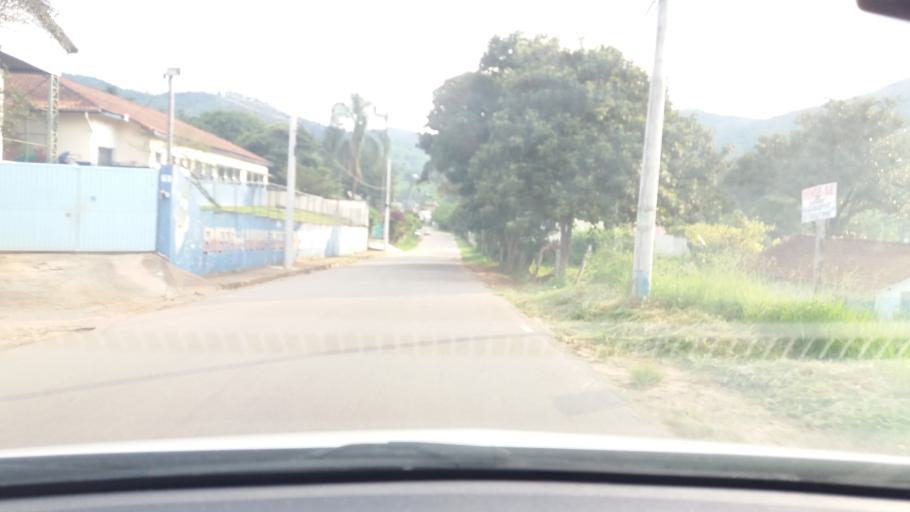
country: BR
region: Sao Paulo
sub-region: Bom Jesus Dos Perdoes
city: Bom Jesus dos Perdoes
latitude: -23.1683
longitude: -46.4786
